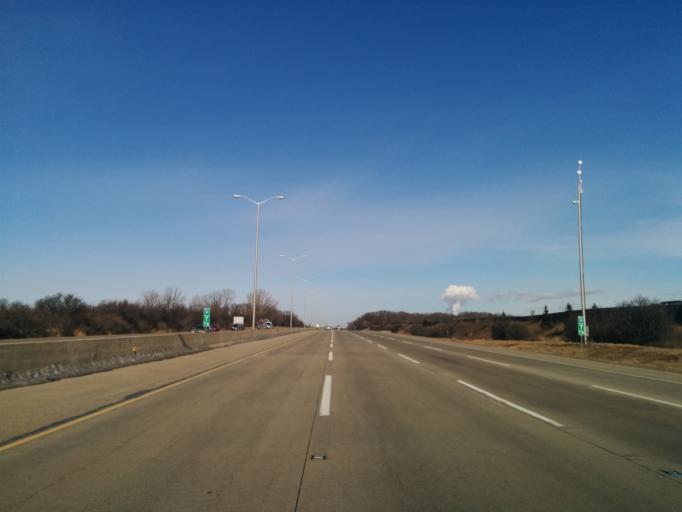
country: US
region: Illinois
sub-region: Lake County
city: Grandwood Park
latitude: 42.3968
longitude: -87.9487
